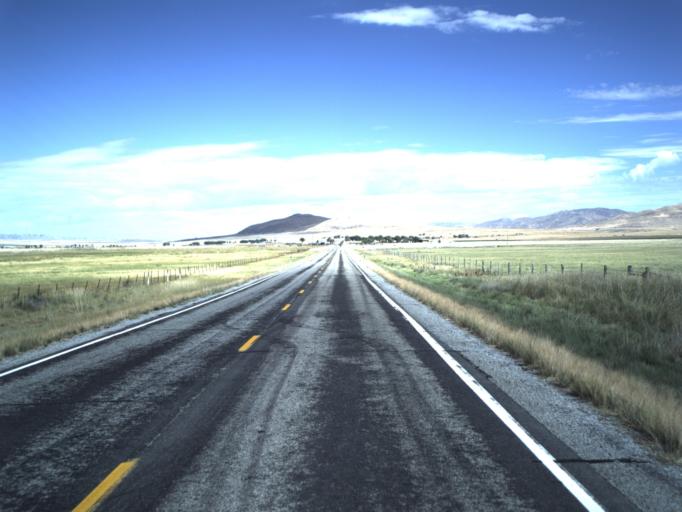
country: US
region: Utah
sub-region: Box Elder County
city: Tremonton
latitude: 41.7532
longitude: -112.4346
